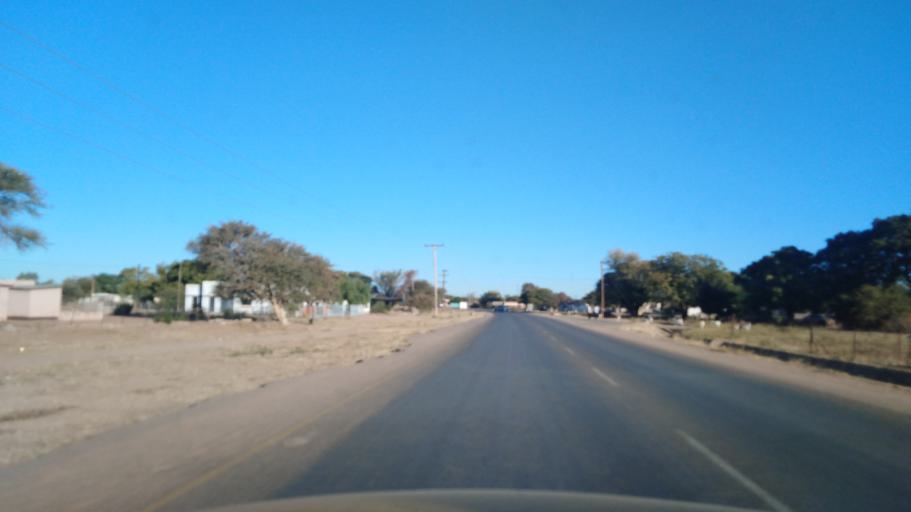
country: BW
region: Central
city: Mahalapye
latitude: -23.0973
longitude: 26.8271
